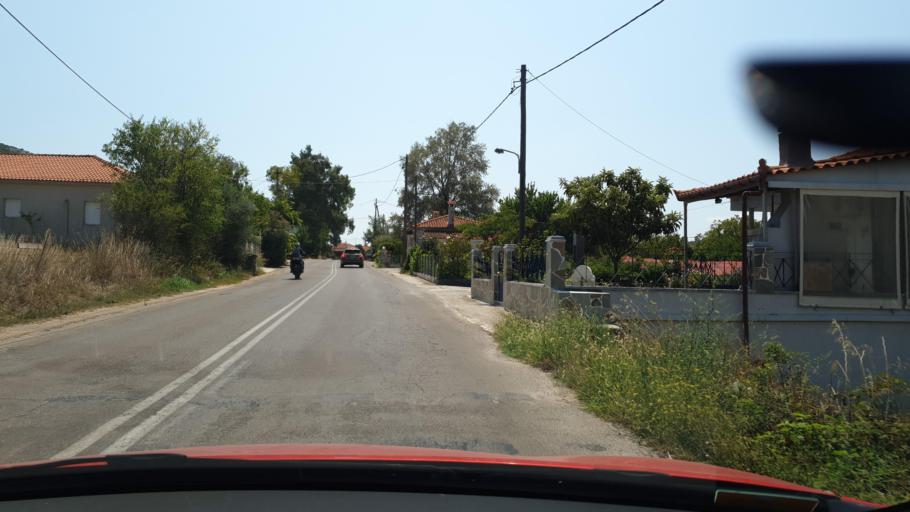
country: GR
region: Central Greece
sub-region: Nomos Evvoias
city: Oxilithos
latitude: 38.4818
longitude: 24.1180
